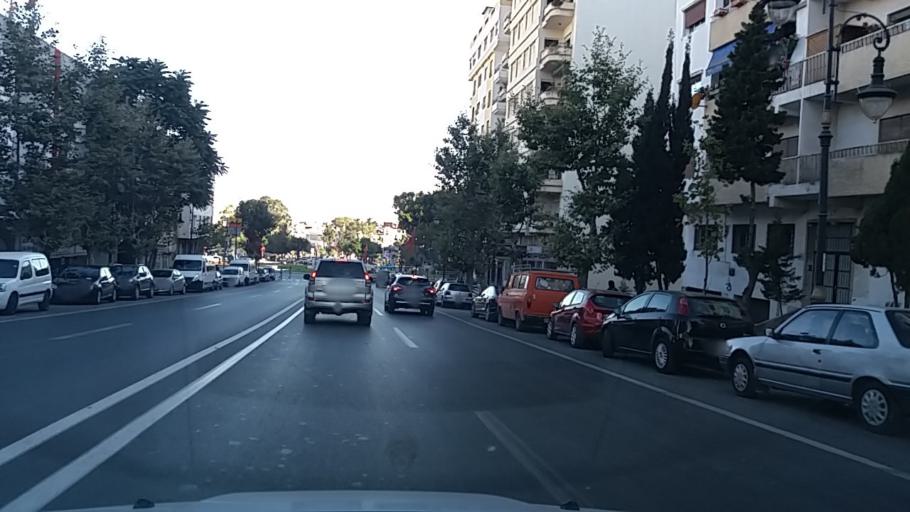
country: MA
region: Tanger-Tetouan
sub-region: Tanger-Assilah
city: Tangier
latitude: 35.7787
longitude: -5.8198
